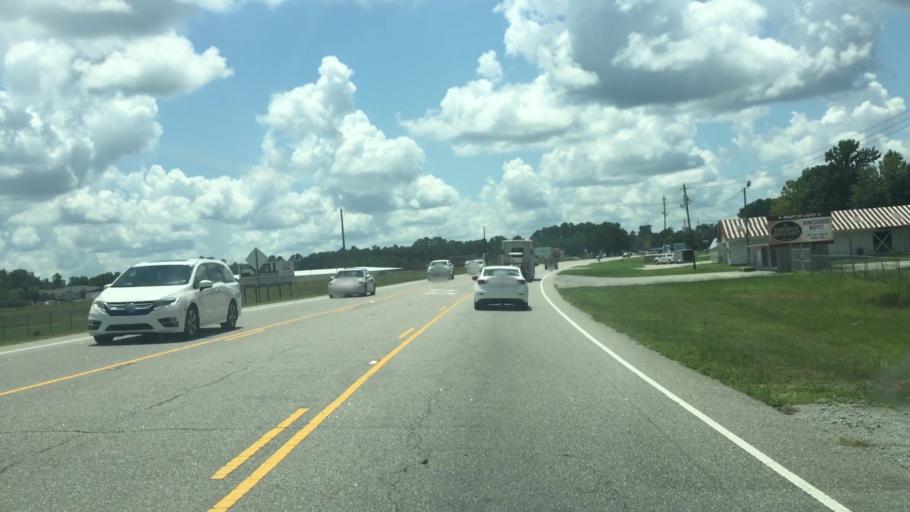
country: US
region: North Carolina
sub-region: Columbus County
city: Tabor City
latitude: 34.1439
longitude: -78.8646
